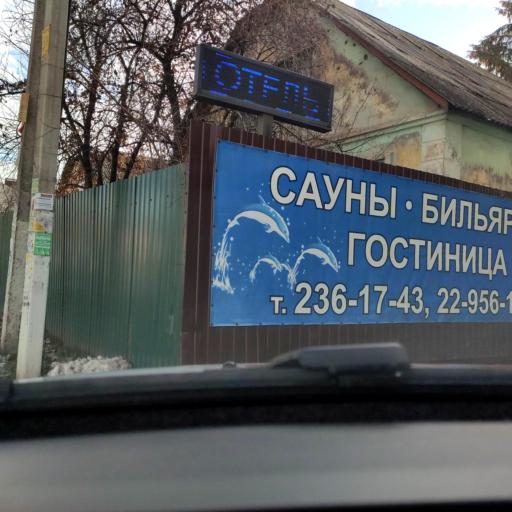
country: RU
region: Voronezj
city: Voronezh
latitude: 51.6356
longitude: 39.1813
